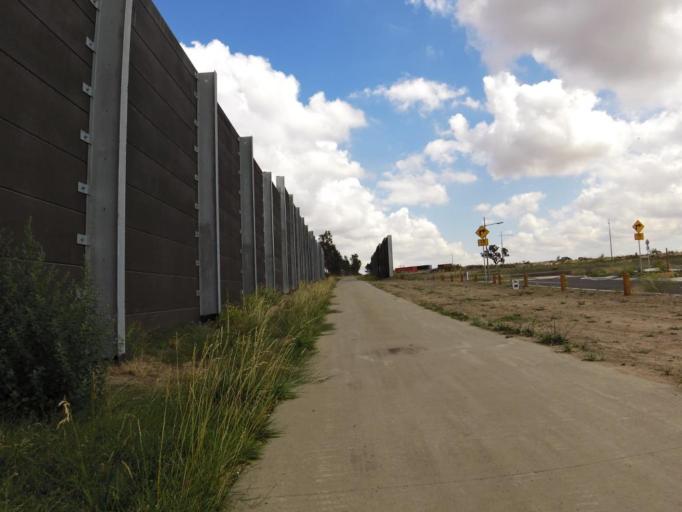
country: AU
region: Victoria
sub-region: Hume
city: Craigieburn
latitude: -37.6206
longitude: 144.9922
